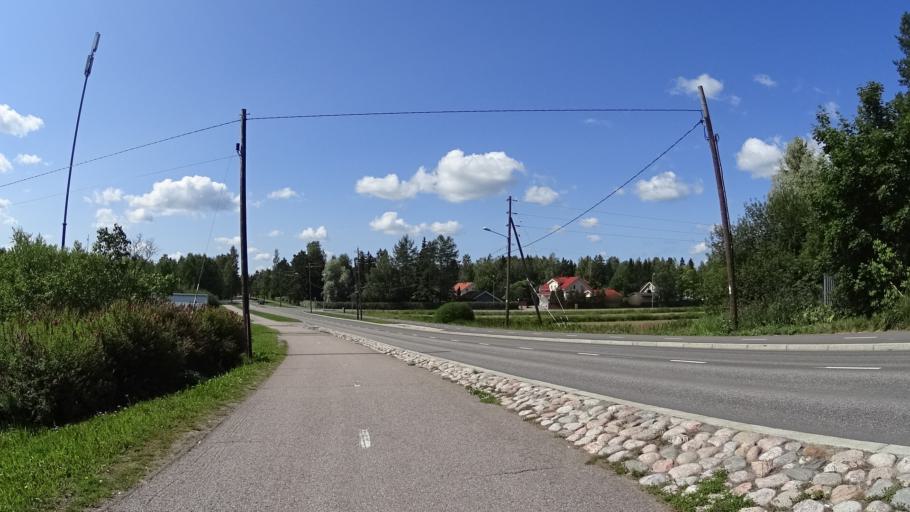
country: FI
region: Uusimaa
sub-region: Helsinki
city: Jaervenpaeae
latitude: 60.4698
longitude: 25.0732
